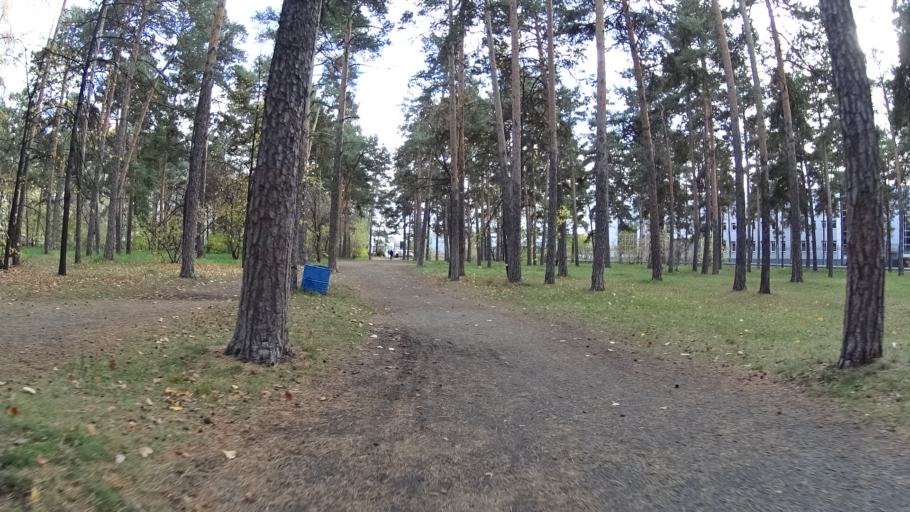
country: RU
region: Chelyabinsk
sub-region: Gorod Chelyabinsk
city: Chelyabinsk
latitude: 55.1617
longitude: 61.3641
